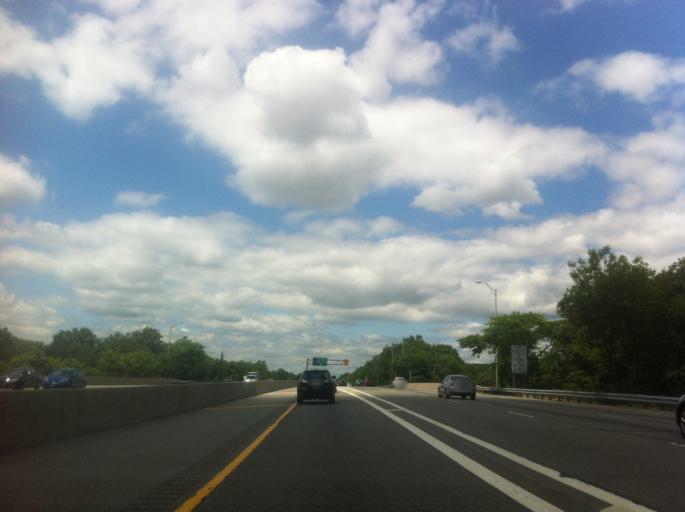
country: US
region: New York
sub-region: Suffolk County
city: Islandia
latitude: 40.8091
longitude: -73.1841
